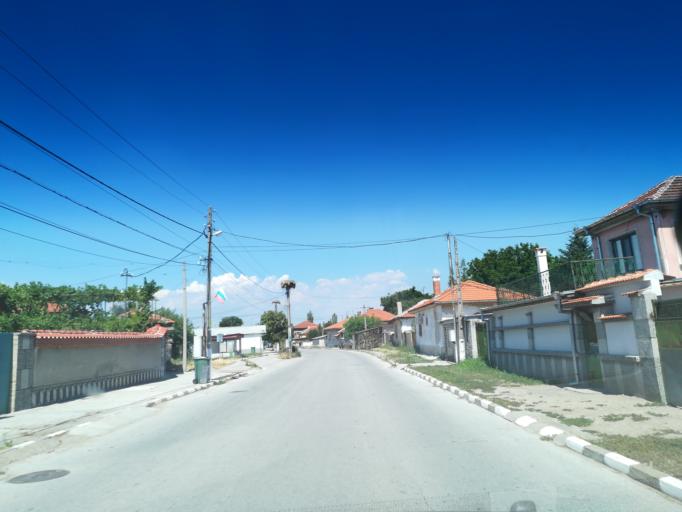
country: BG
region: Plovdiv
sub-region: Obshtina Sadovo
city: Sadovo
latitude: 42.0284
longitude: 25.1126
